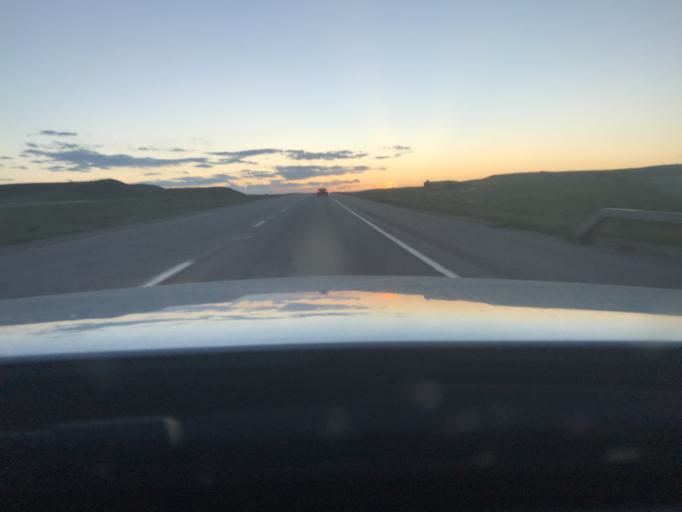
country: US
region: Wyoming
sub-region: Converse County
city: Glenrock
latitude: 42.8337
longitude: -105.8458
